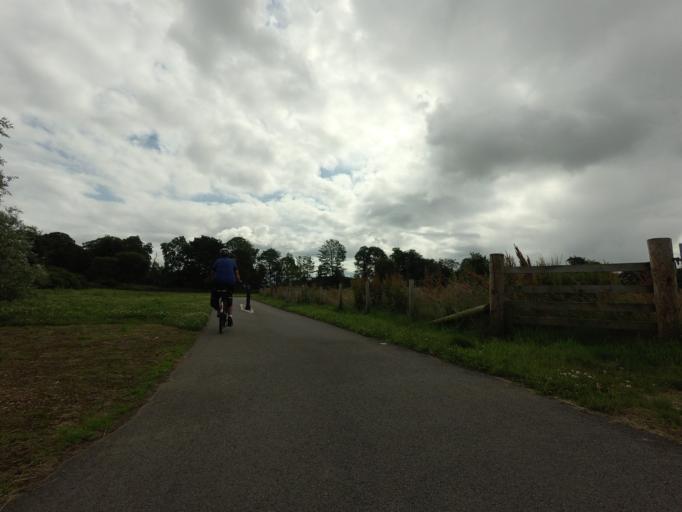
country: GB
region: Scotland
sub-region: Moray
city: Lhanbryd
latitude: 57.6428
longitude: -3.2643
